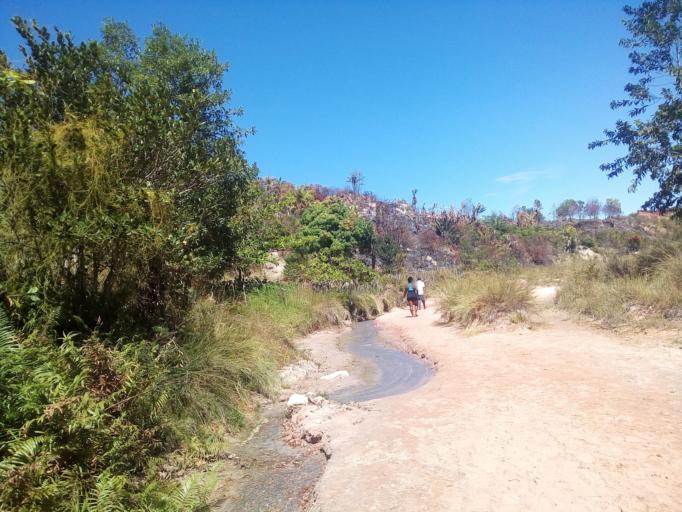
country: MG
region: Boeny
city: Mahajanga
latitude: -15.6313
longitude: 46.3506
